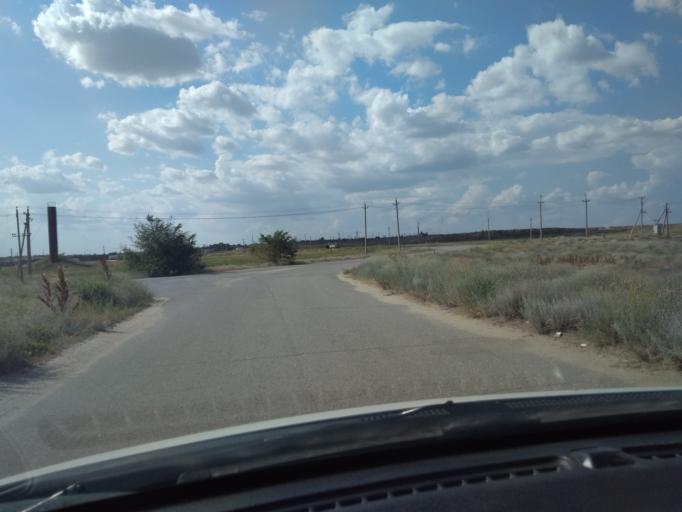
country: RU
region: Volgograd
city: Vodstroy
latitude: 48.8044
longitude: 44.5292
